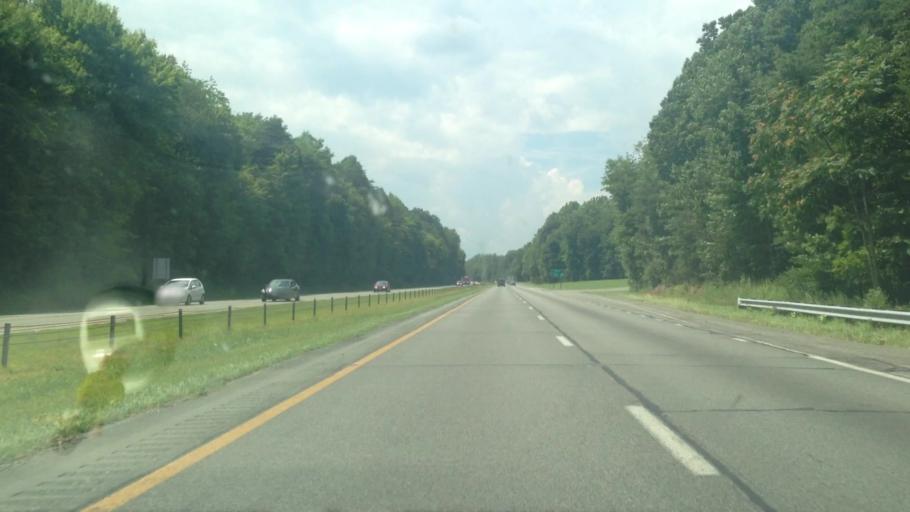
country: US
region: North Carolina
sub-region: Surry County
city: Pilot Mountain
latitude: 36.3365
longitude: -80.4557
